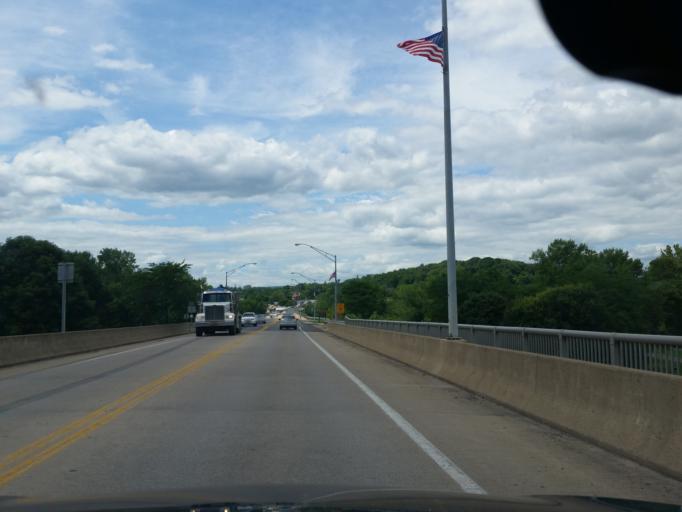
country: US
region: Pennsylvania
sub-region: Northumberland County
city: Milton
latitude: 41.0175
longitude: -76.8611
